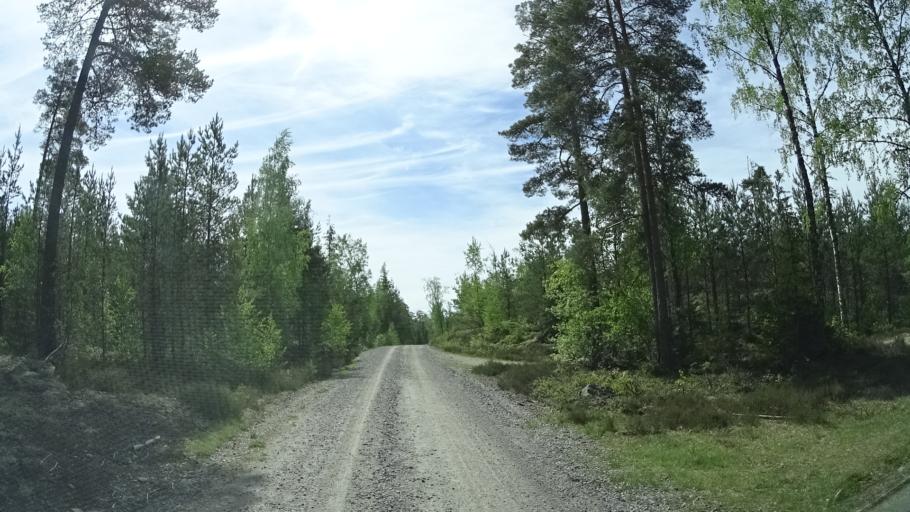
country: SE
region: OEstergoetland
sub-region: Finspangs Kommun
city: Finspang
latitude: 58.7824
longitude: 15.8467
